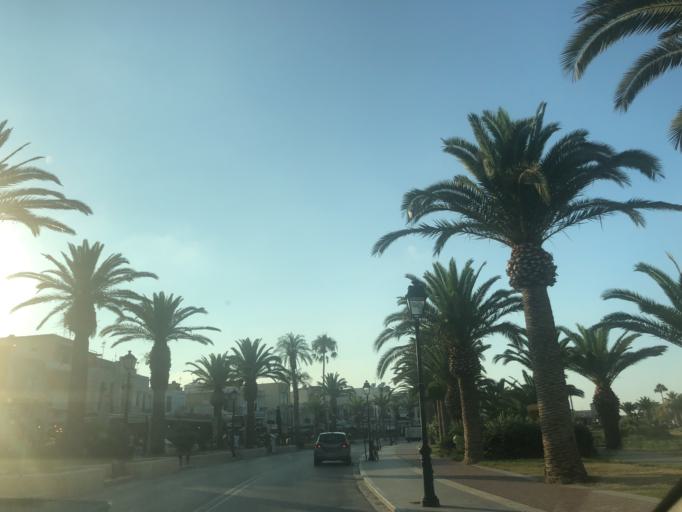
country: GR
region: Crete
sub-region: Nomos Rethymnis
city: Rethymno
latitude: 35.3682
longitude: 24.4773
